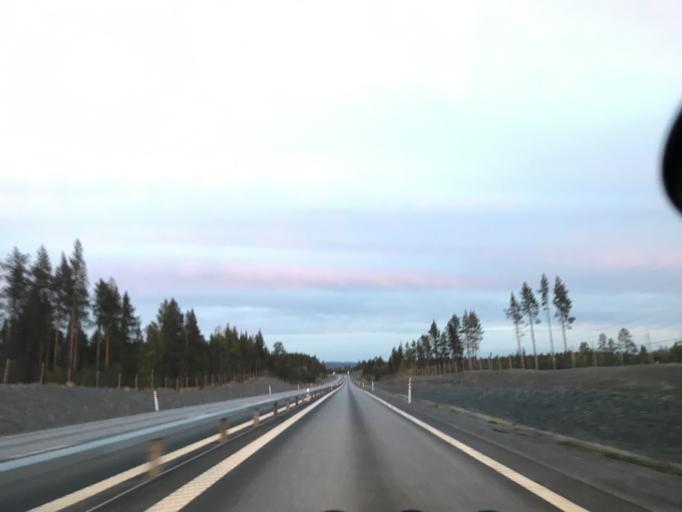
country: SE
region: Norrbotten
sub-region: Gallivare Kommun
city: Malmberget
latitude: 67.6814
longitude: 20.8737
